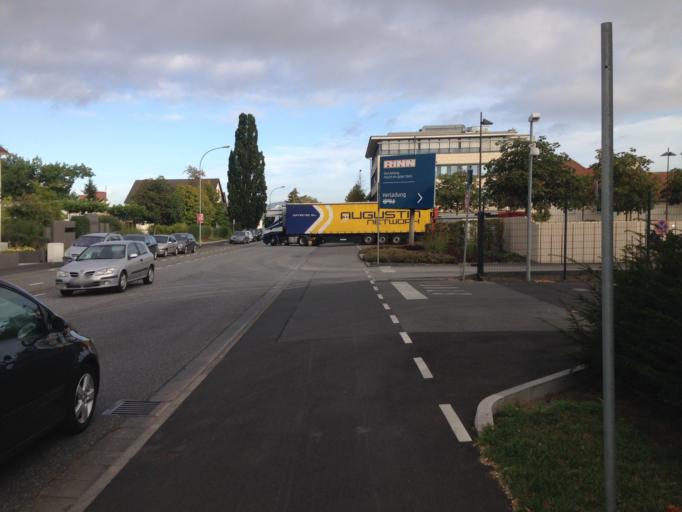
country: DE
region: Hesse
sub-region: Regierungsbezirk Giessen
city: Heuchelheim
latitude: 50.5945
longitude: 8.6304
